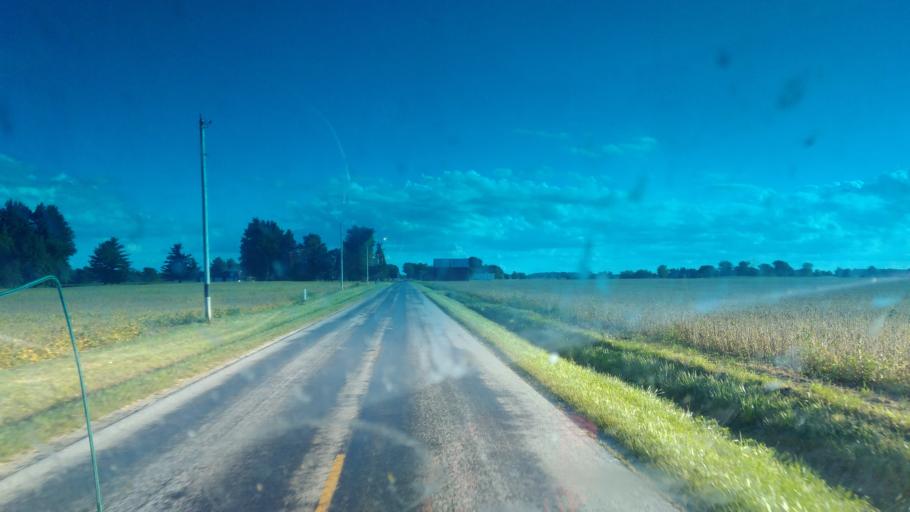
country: US
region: Ohio
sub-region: Wyandot County
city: Carey
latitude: 40.9259
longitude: -83.4009
